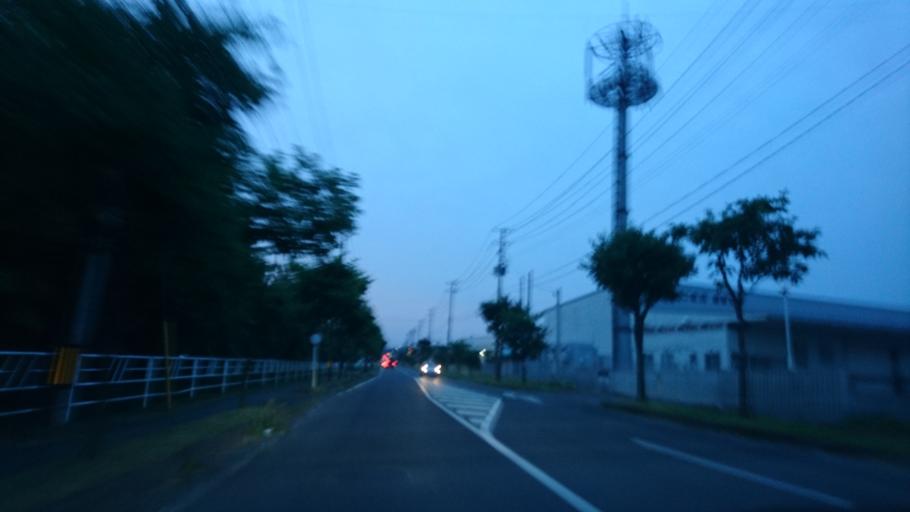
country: JP
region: Iwate
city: Ichinoseki
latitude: 38.8031
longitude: 141.0694
